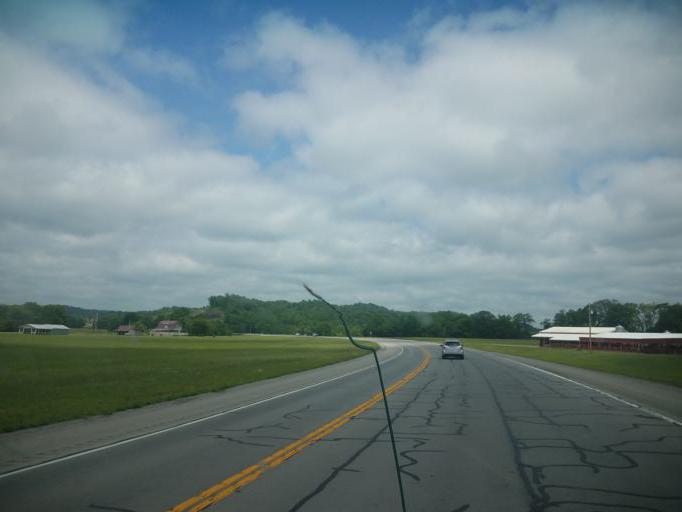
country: US
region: Kentucky
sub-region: Metcalfe County
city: Edmonton
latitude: 36.8443
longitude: -85.5371
